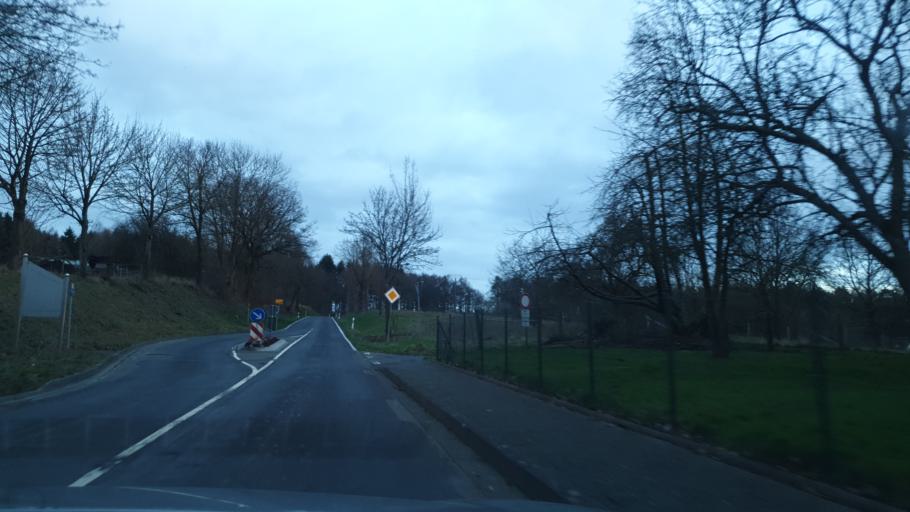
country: DE
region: Rheinland-Pfalz
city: Fluterschen
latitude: 50.6656
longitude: 7.6305
